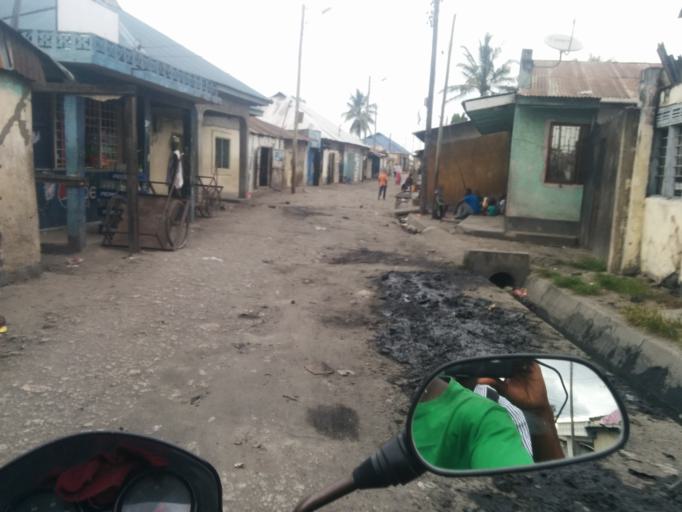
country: TZ
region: Dar es Salaam
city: Dar es Salaam
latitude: -6.8357
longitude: 39.2779
